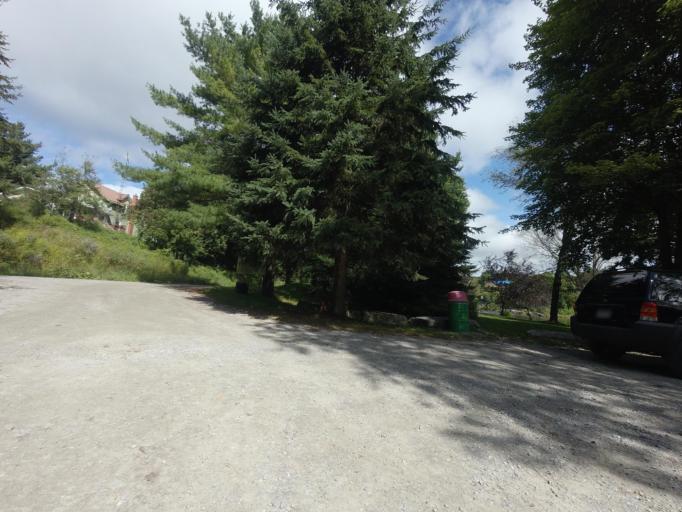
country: CA
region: Ontario
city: Omemee
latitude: 44.7790
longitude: -78.6526
